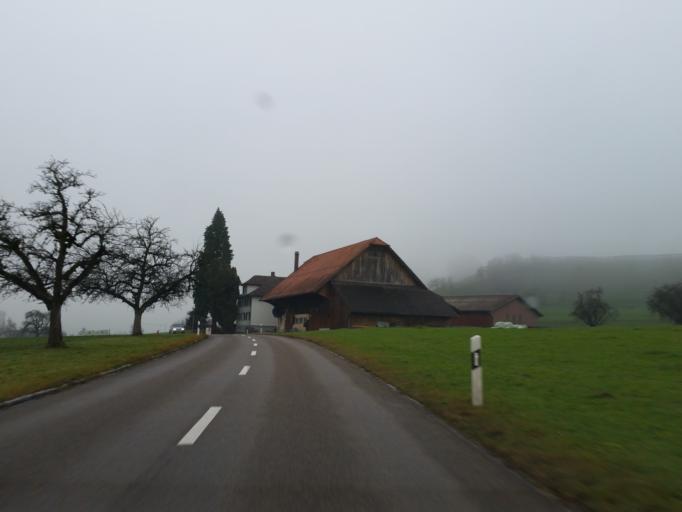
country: CH
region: Saint Gallen
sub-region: Wahlkreis Wil
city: Niederhelfenschwil
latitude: 47.4893
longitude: 9.1703
